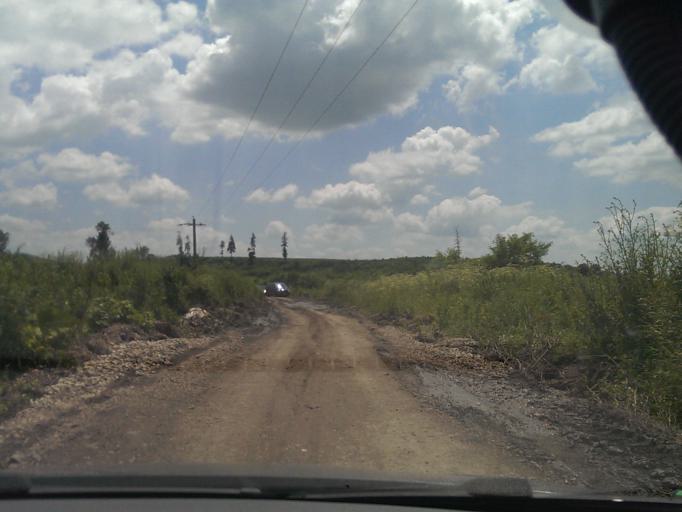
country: RO
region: Cluj
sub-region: Comuna Bontida
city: Rascruci
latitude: 46.9116
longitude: 23.8039
